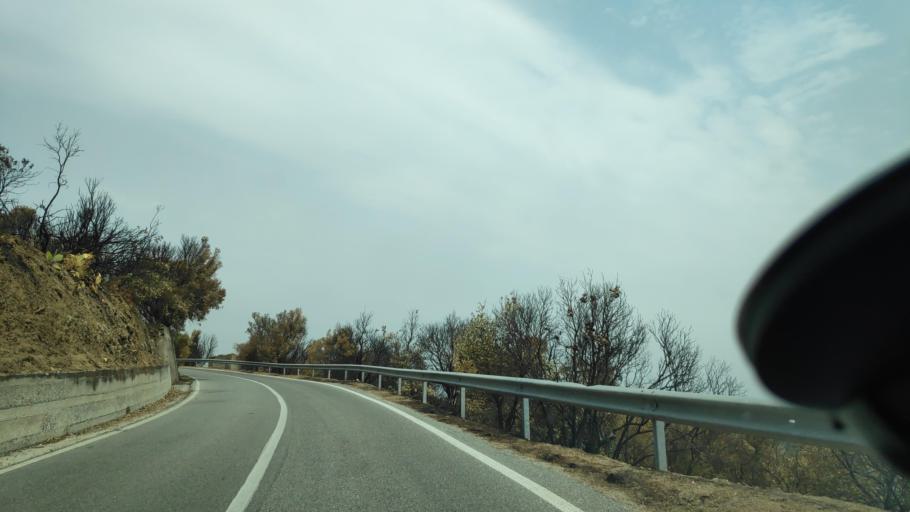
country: IT
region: Calabria
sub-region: Provincia di Catanzaro
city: Sant'Andrea Apostolo dello Ionio
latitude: 38.6452
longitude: 16.5311
